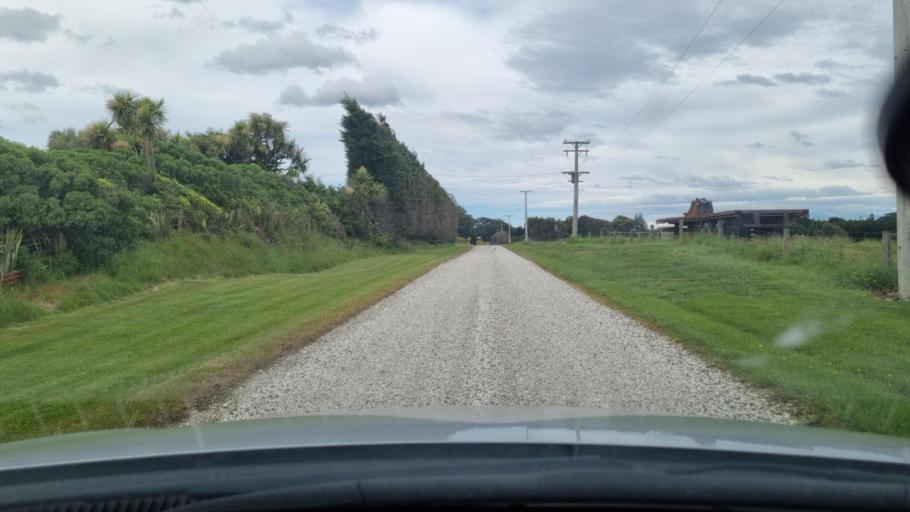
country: NZ
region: Southland
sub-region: Invercargill City
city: Invercargill
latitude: -46.4056
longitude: 168.2600
